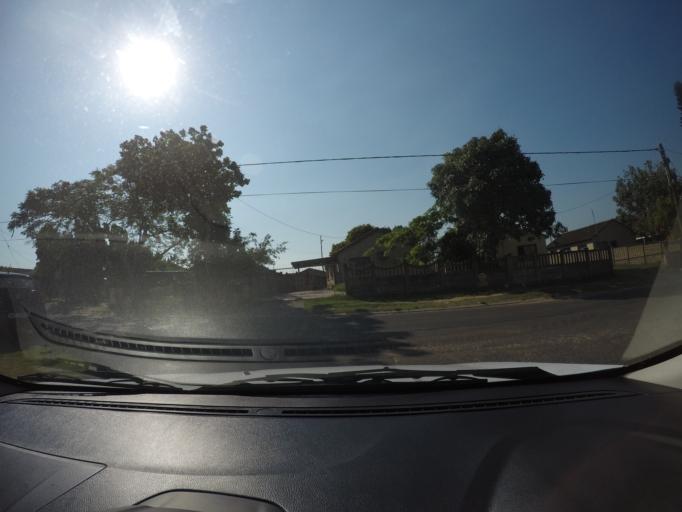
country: ZA
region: KwaZulu-Natal
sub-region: uThungulu District Municipality
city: Richards Bay
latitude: -28.7199
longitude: 32.0430
